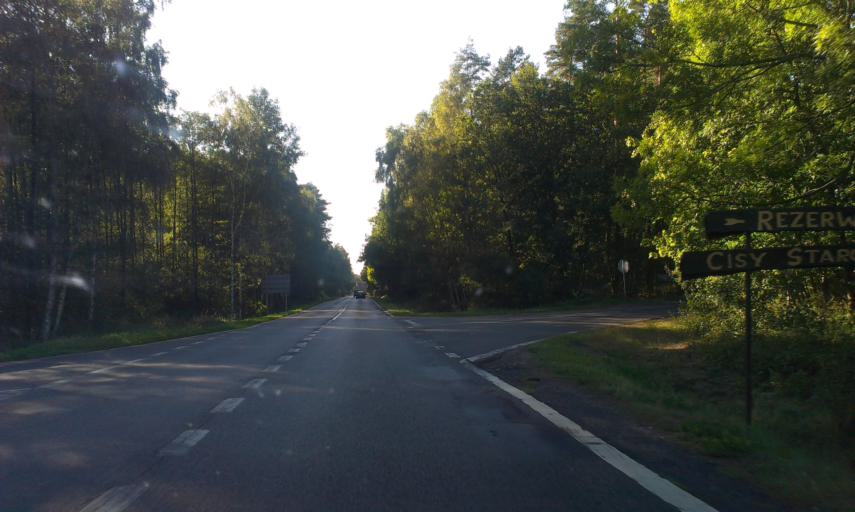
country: PL
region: Kujawsko-Pomorskie
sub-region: Powiat swiecki
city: Swiekatowo
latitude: 53.4879
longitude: 18.1099
